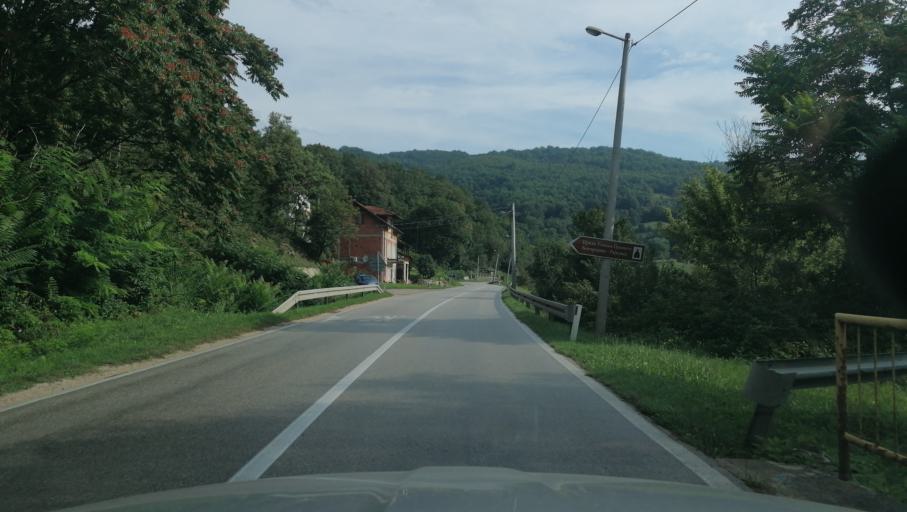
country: BA
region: Republika Srpska
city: Hiseti
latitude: 44.6727
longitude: 17.1457
